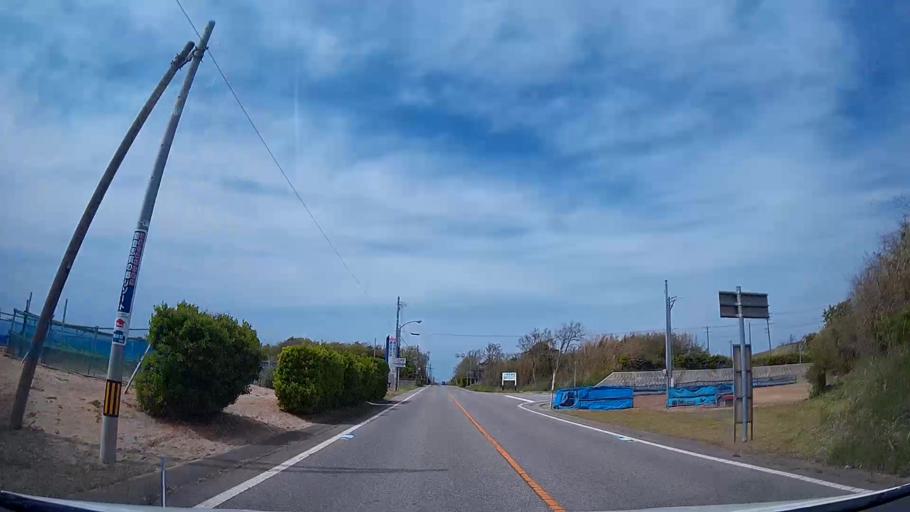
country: JP
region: Ishikawa
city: Hakui
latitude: 36.9636
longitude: 136.7734
